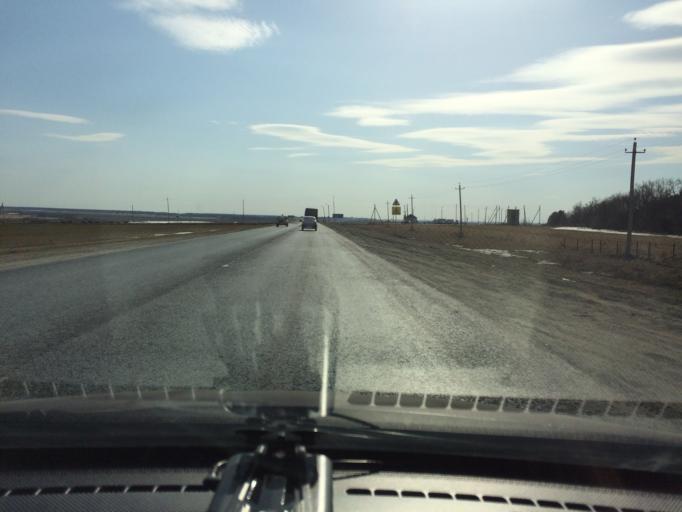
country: RU
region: Mariy-El
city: Yoshkar-Ola
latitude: 56.6986
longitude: 48.0641
